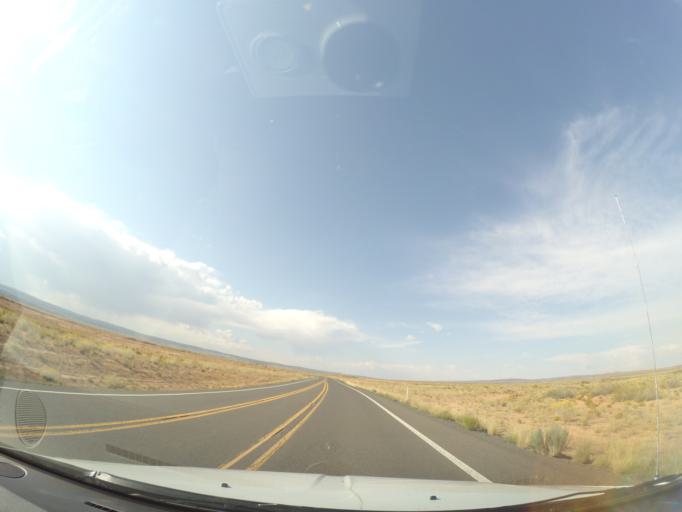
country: US
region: Arizona
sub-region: Coconino County
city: Tuba City
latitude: 36.3949
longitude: -111.4174
